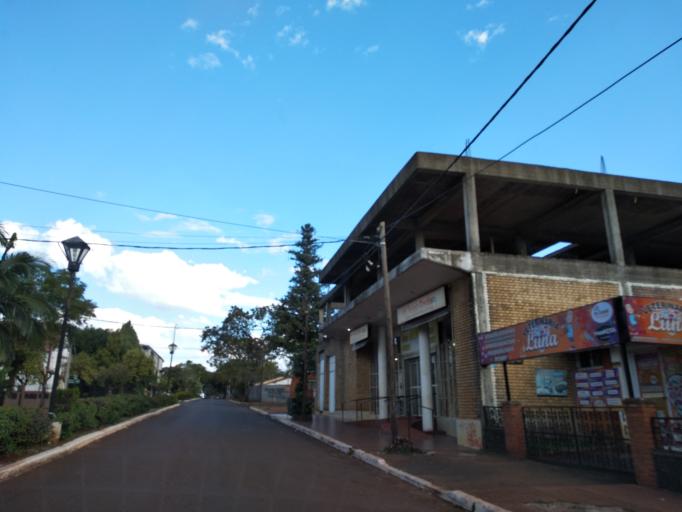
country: AR
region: Misiones
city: Jardin America
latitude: -27.0410
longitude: -55.2271
